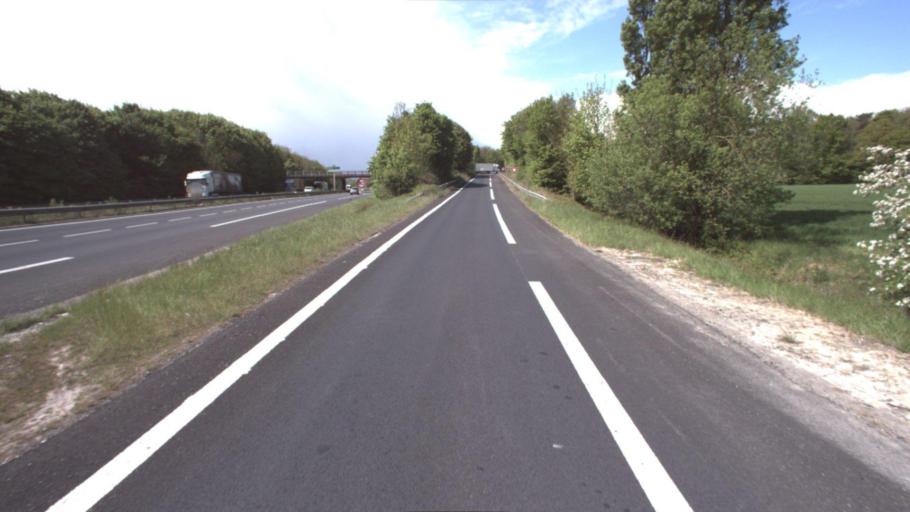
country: FR
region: Ile-de-France
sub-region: Departement de Seine-et-Marne
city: Fontenay-Tresigny
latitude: 48.7170
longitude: 2.8491
